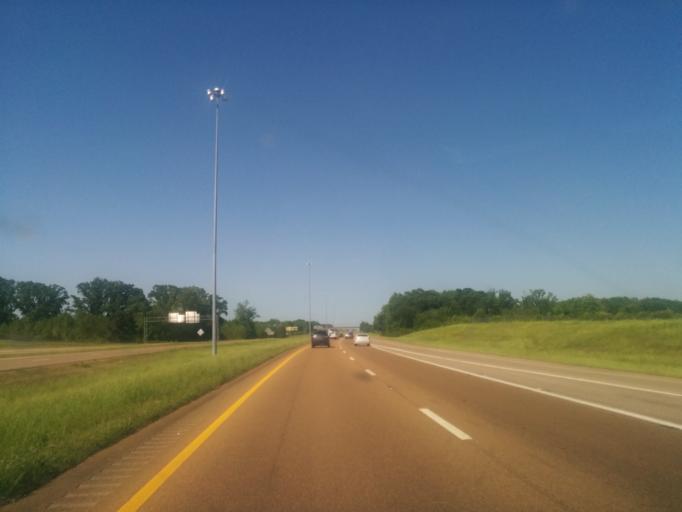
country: US
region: Mississippi
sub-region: Madison County
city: Madison
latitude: 32.5434
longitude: -90.0934
